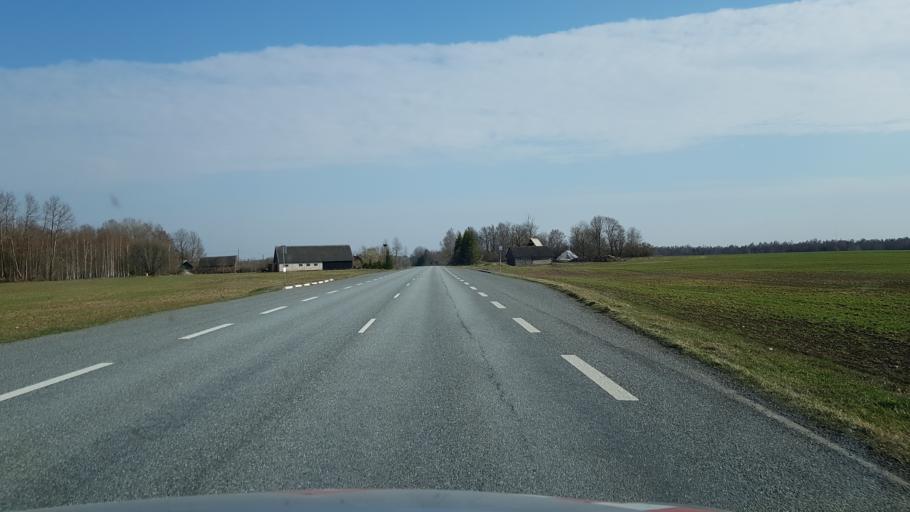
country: EE
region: Laeaene-Virumaa
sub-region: Kadrina vald
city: Kadrina
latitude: 59.3746
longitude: 26.0990
